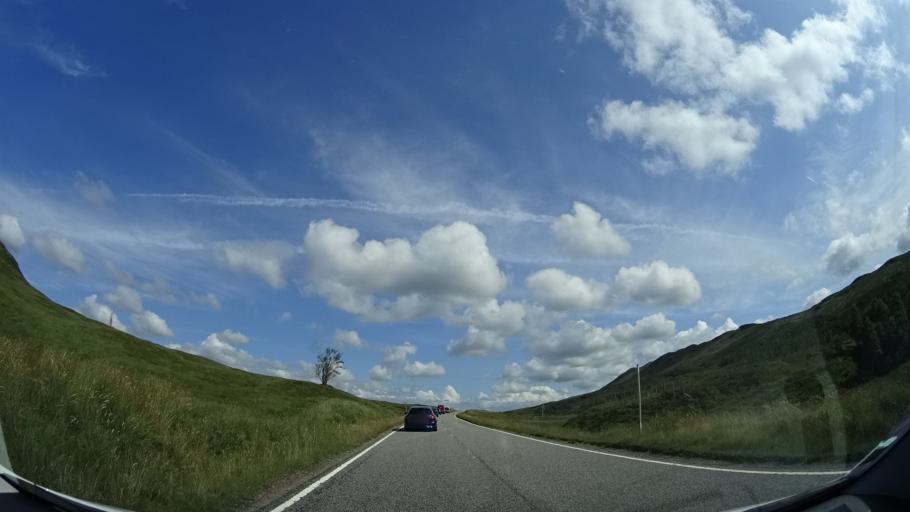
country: GB
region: Scotland
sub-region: Highland
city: Spean Bridge
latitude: 56.5802
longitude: -4.7547
